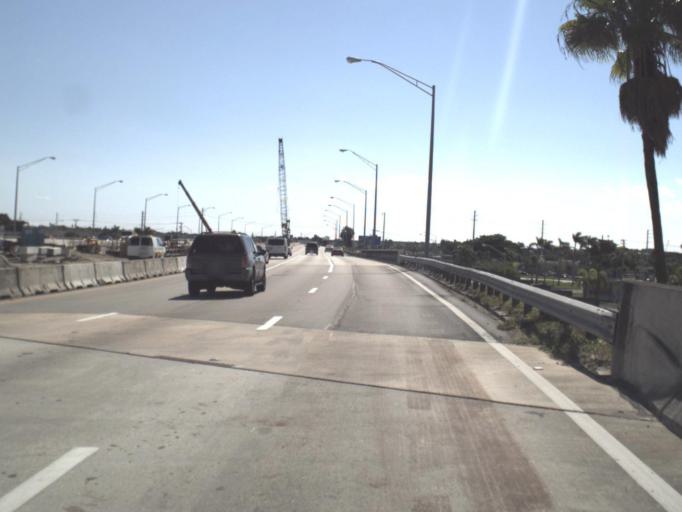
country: US
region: Florida
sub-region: Miami-Dade County
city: South Miami Heights
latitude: 25.5976
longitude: -80.3751
